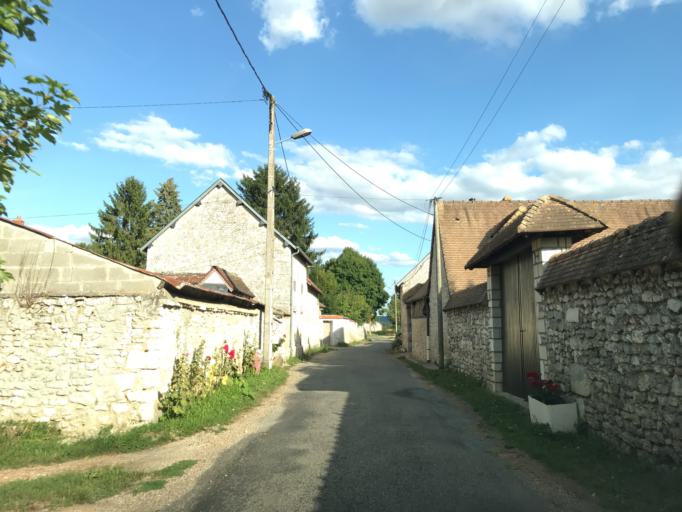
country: FR
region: Haute-Normandie
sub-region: Departement de l'Eure
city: Courcelles-sur-Seine
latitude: 49.1690
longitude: 1.4010
